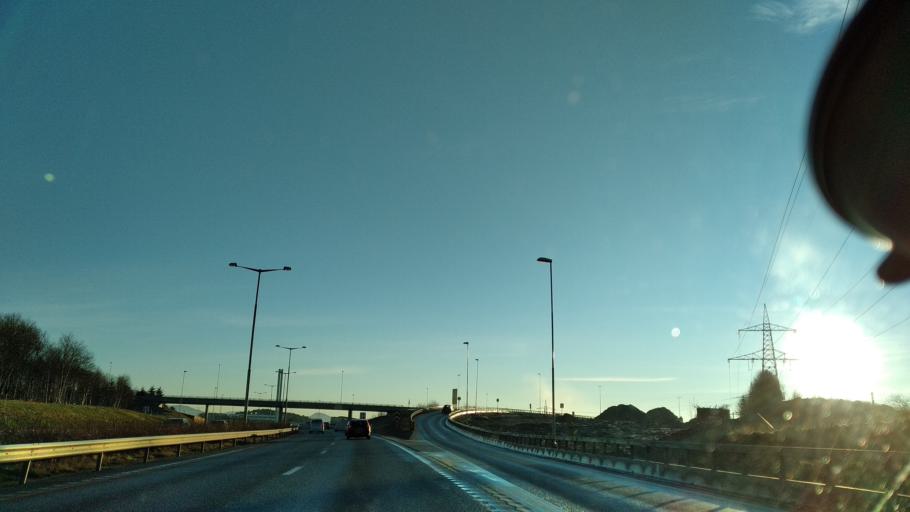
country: NO
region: Rogaland
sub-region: Sola
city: Sola
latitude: 58.9106
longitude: 5.6958
